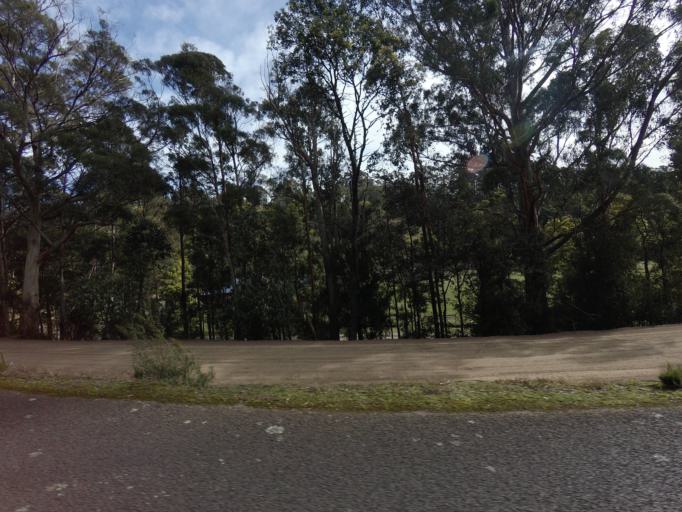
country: AU
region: Tasmania
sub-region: Kingborough
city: Margate
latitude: -43.0005
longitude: 147.1769
